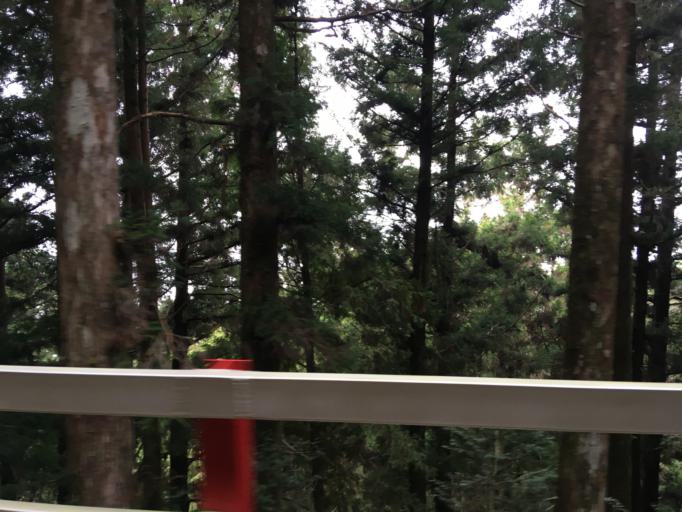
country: TW
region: Taiwan
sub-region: Yilan
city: Yilan
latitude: 24.4802
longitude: 121.5369
